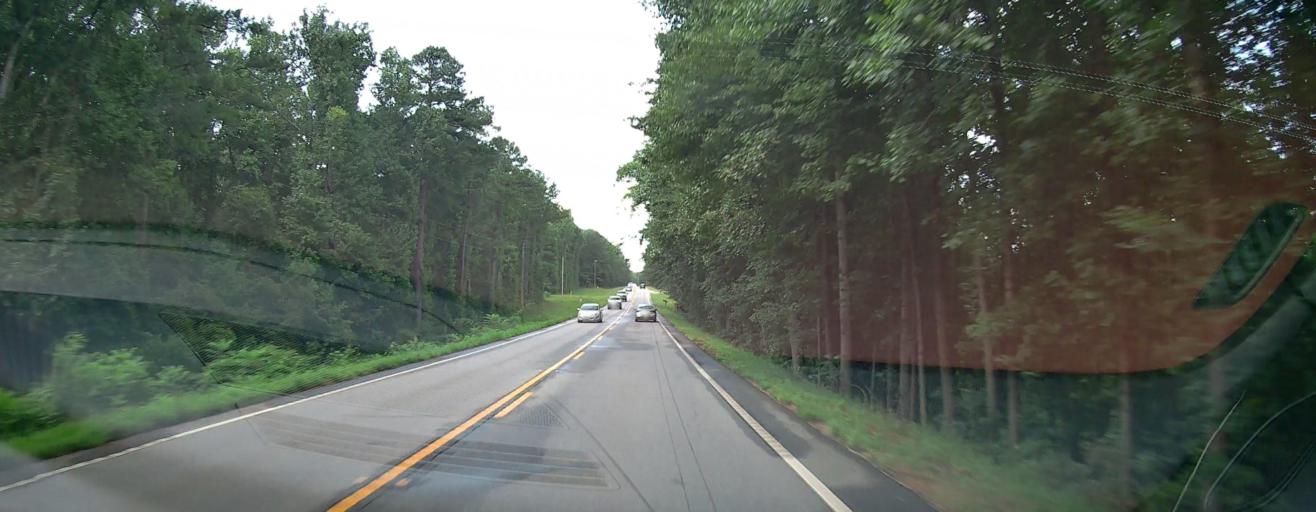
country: US
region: Georgia
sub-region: Coweta County
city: Senoia
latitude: 33.2622
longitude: -84.5546
